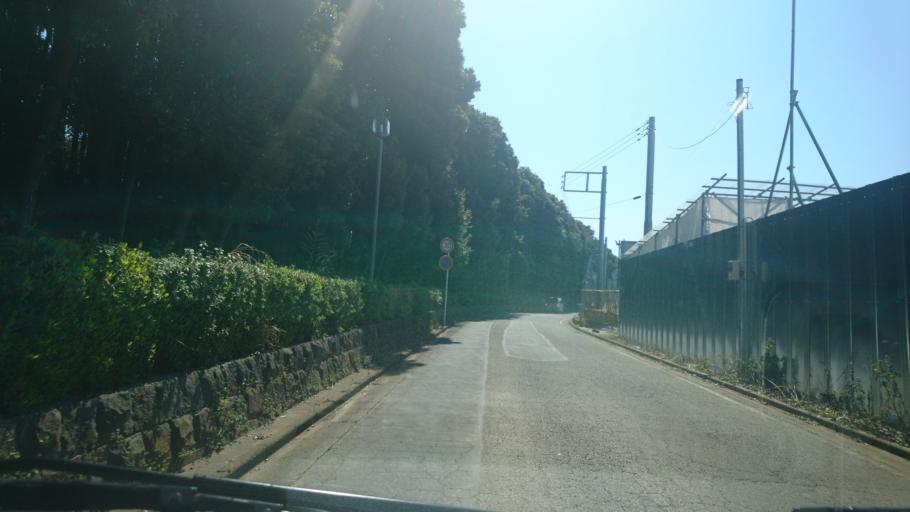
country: JP
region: Kanagawa
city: Fujisawa
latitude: 35.3896
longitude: 139.4250
